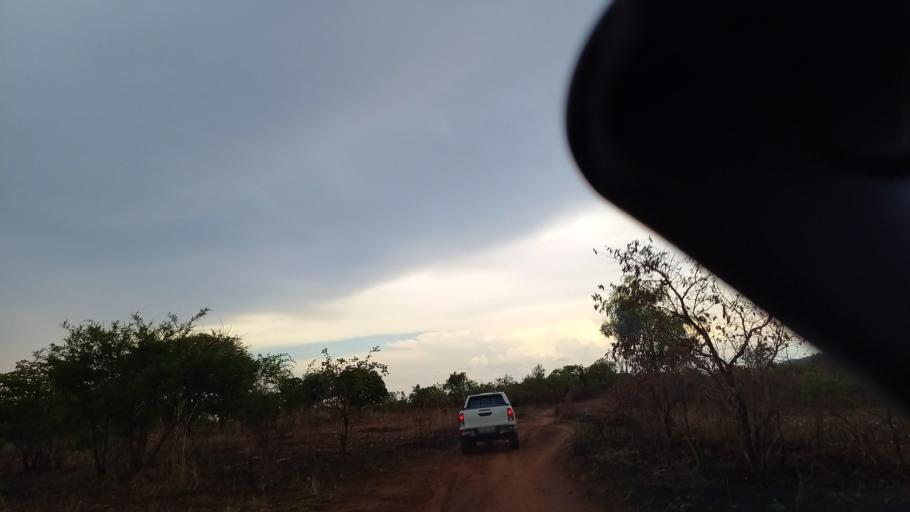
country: ZM
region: Lusaka
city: Kafue
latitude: -16.0294
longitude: 28.3015
